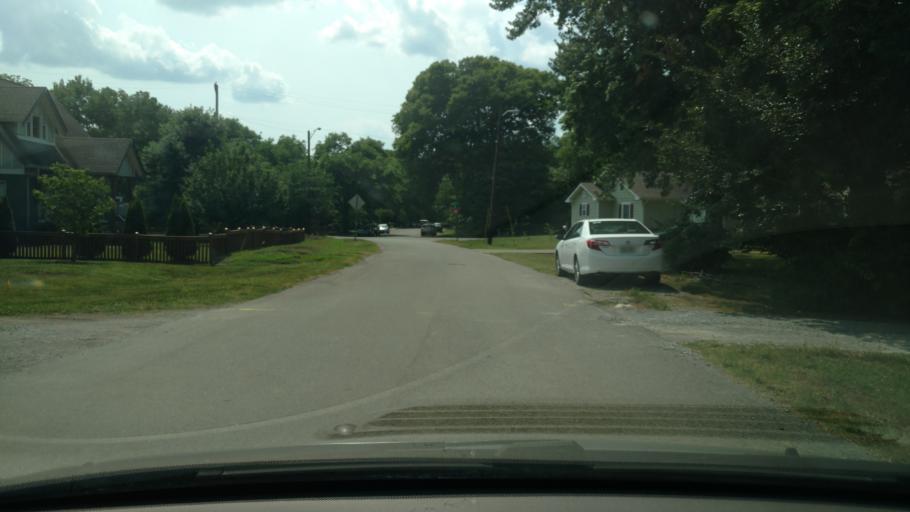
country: US
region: Tennessee
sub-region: Davidson County
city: Nashville
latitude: 36.1909
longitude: -86.7384
